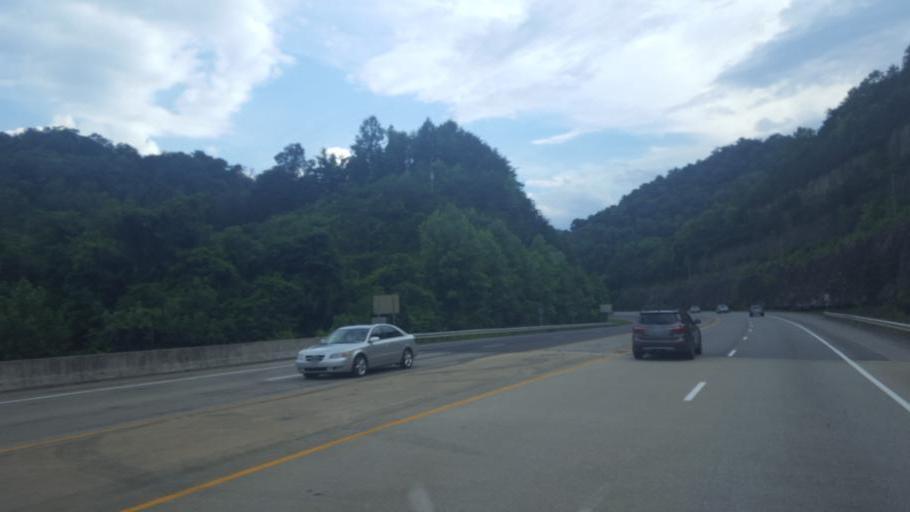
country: US
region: Kentucky
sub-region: Pike County
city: Pikeville
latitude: 37.4356
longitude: -82.5128
